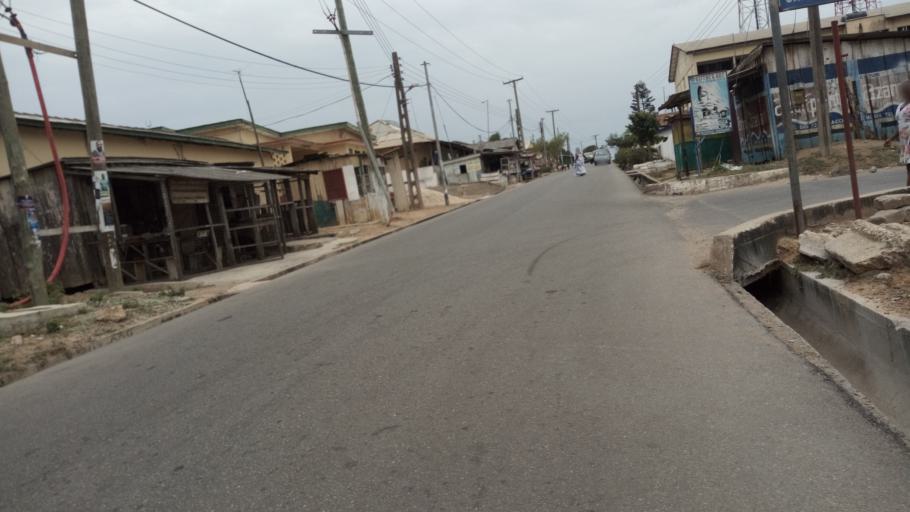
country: GH
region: Central
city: Winneba
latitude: 5.3449
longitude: -0.6259
